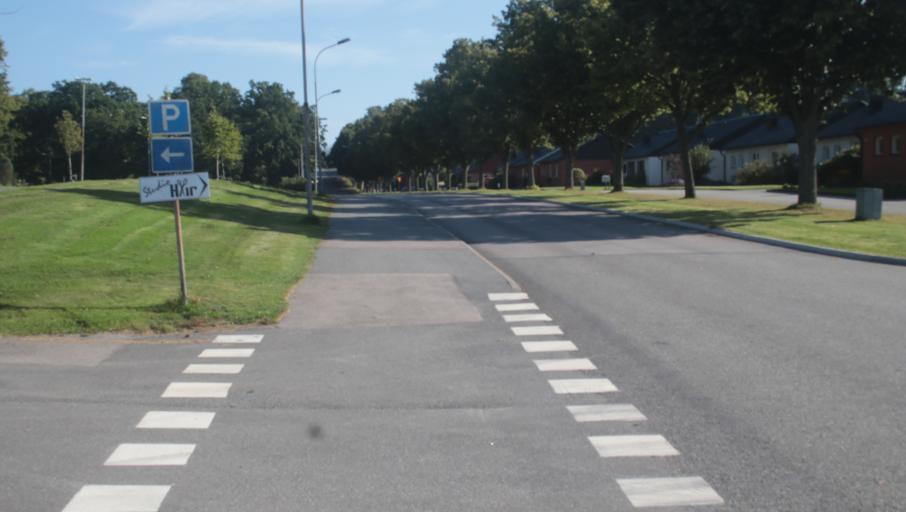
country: SE
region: Blekinge
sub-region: Karlshamns Kommun
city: Karlshamn
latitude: 56.1775
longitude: 14.8487
